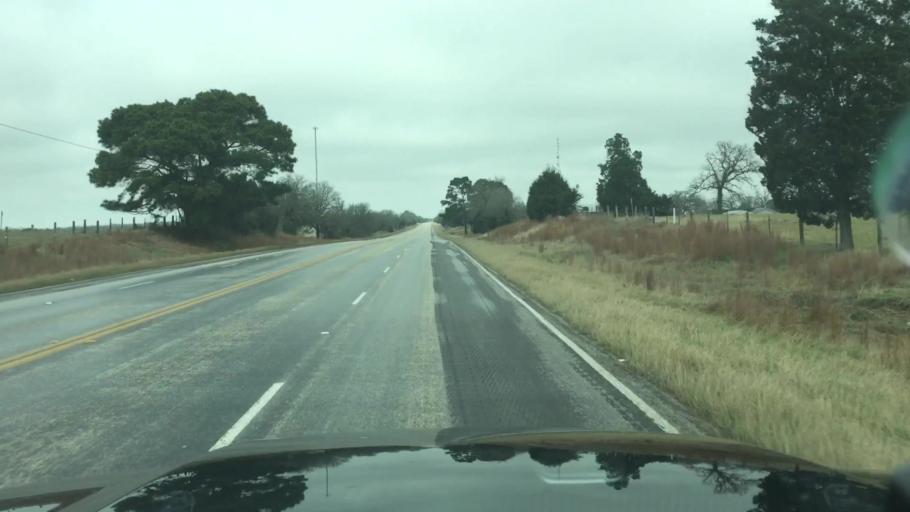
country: US
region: Texas
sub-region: Lee County
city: Giddings
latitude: 30.1018
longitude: -96.9138
